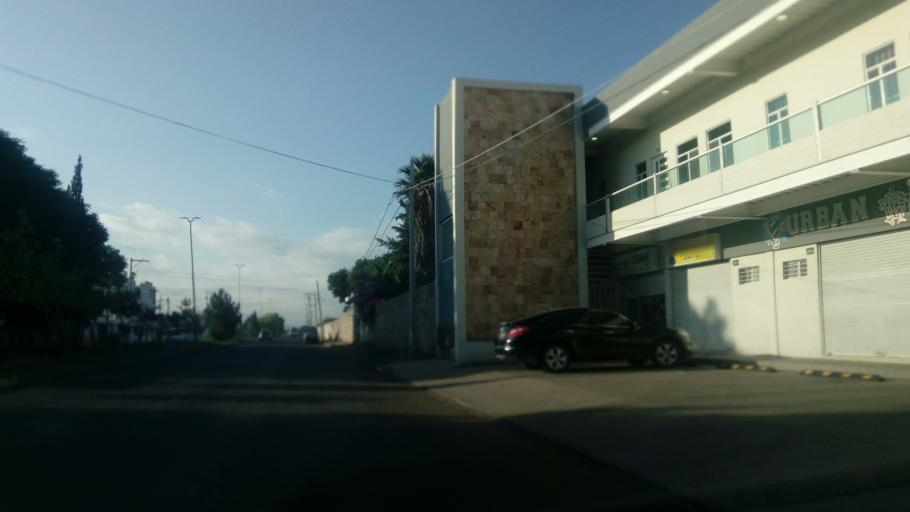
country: MX
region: Durango
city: Victoria de Durango
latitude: 24.0427
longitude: -104.6117
